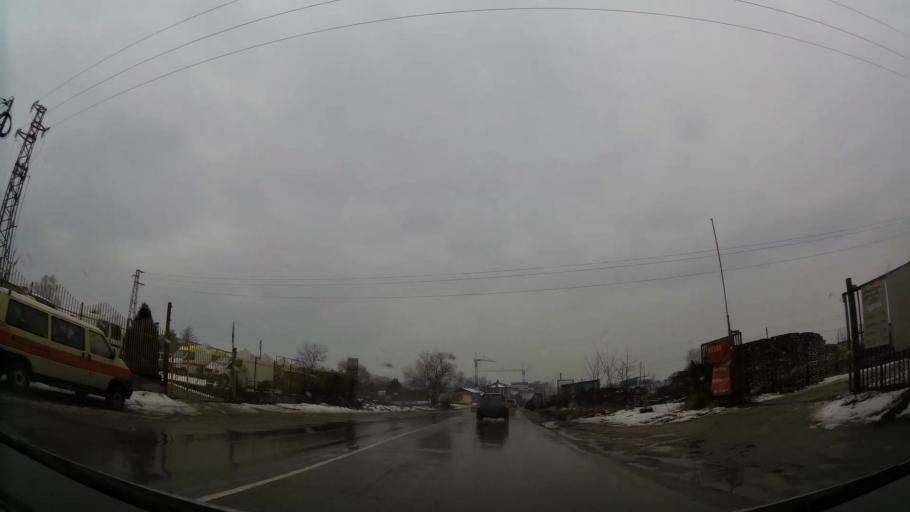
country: BG
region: Sofiya
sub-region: Obshtina Bozhurishte
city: Bozhurishte
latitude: 42.6879
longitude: 23.2316
